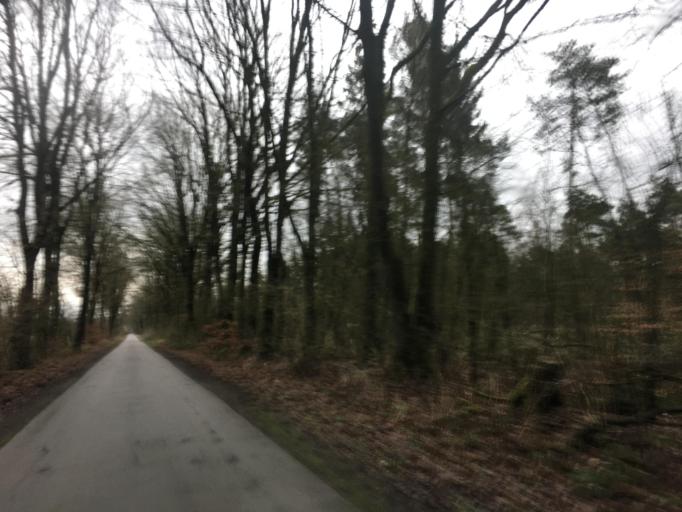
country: DE
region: North Rhine-Westphalia
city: Olfen
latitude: 51.7464
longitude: 7.3104
